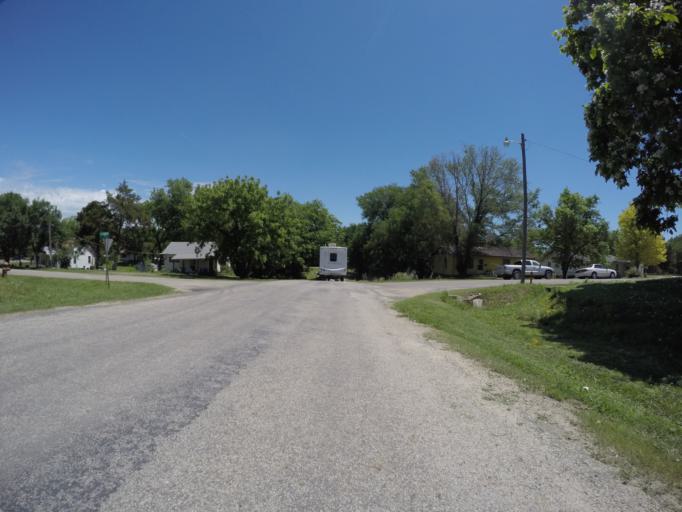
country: US
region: Kansas
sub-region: Jewell County
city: Mankato
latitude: 39.7868
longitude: -98.2062
